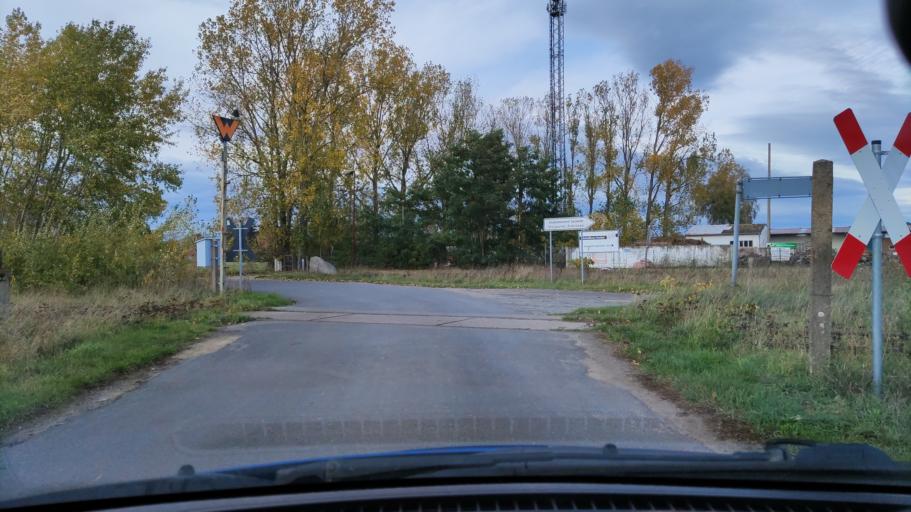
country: DE
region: Saxony-Anhalt
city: Luftkurort Arendsee
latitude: 52.8782
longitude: 11.5020
